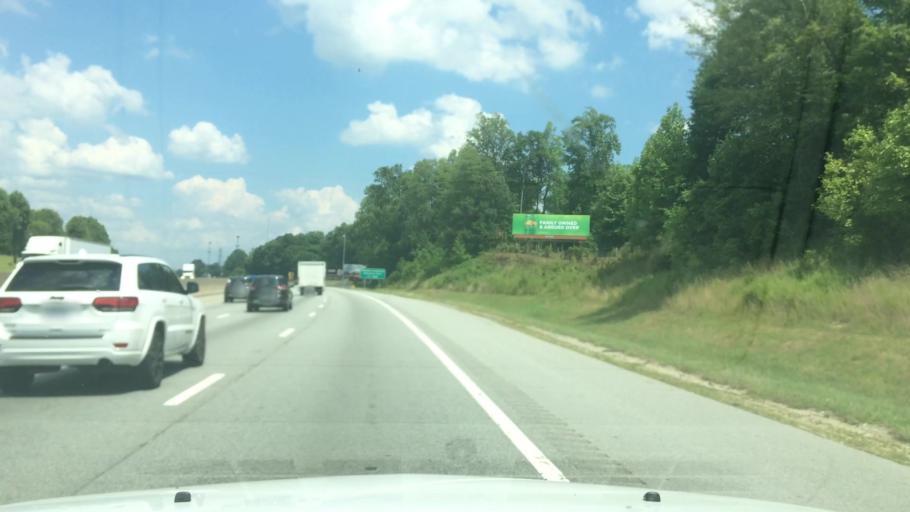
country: US
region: North Carolina
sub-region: Guilford County
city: Greensboro
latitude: 36.0468
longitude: -79.7521
